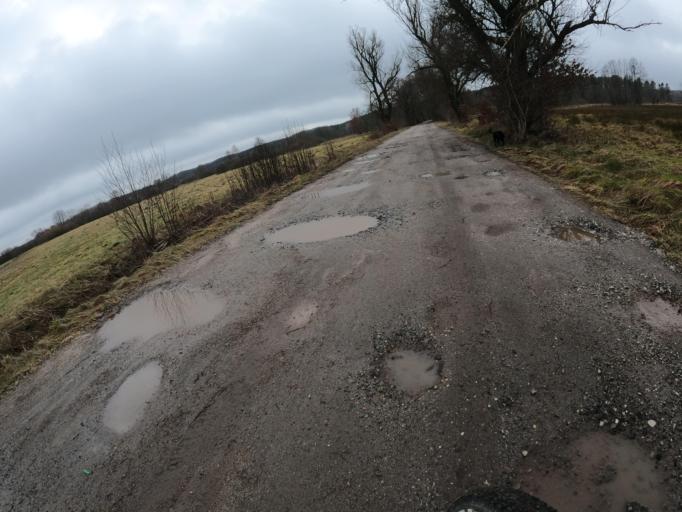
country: PL
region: West Pomeranian Voivodeship
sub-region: Powiat slawienski
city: Slawno
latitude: 54.2542
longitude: 16.6446
